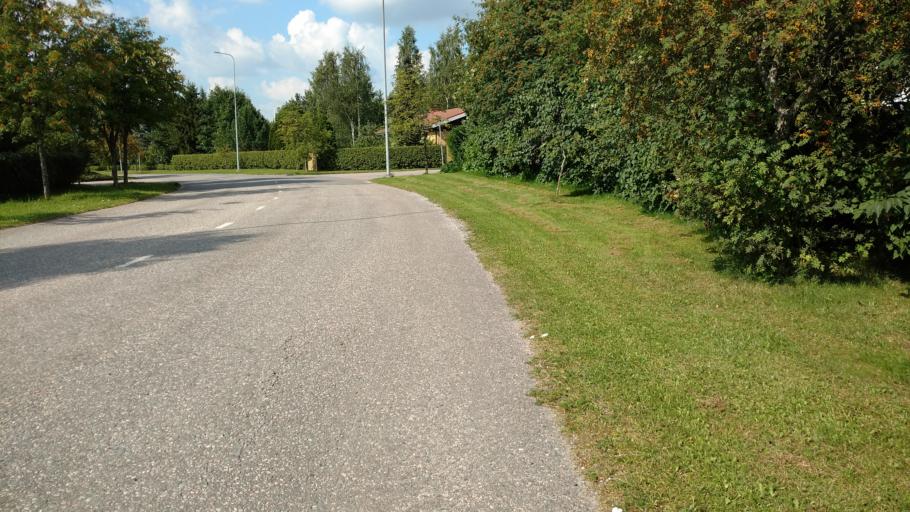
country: FI
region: Varsinais-Suomi
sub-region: Salo
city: Salo
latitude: 60.3950
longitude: 23.1696
